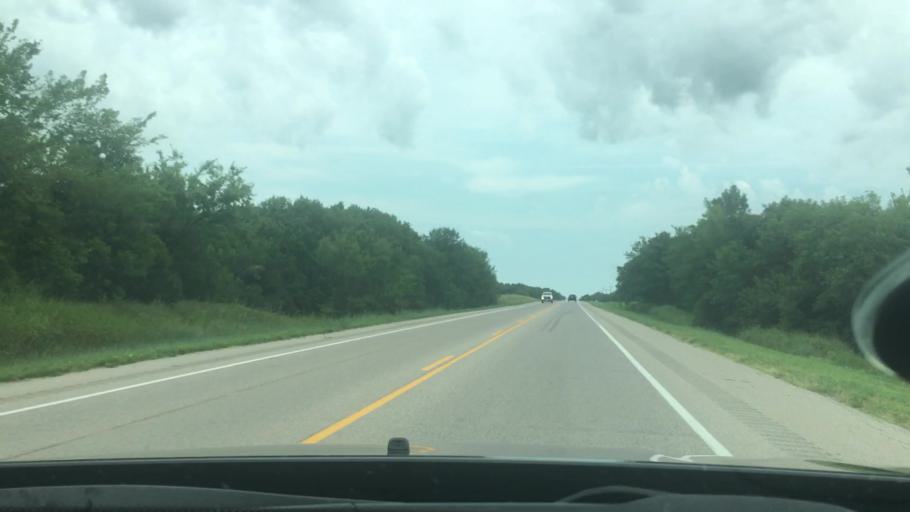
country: US
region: Oklahoma
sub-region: Seminole County
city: Konawa
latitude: 34.9649
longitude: -96.6788
